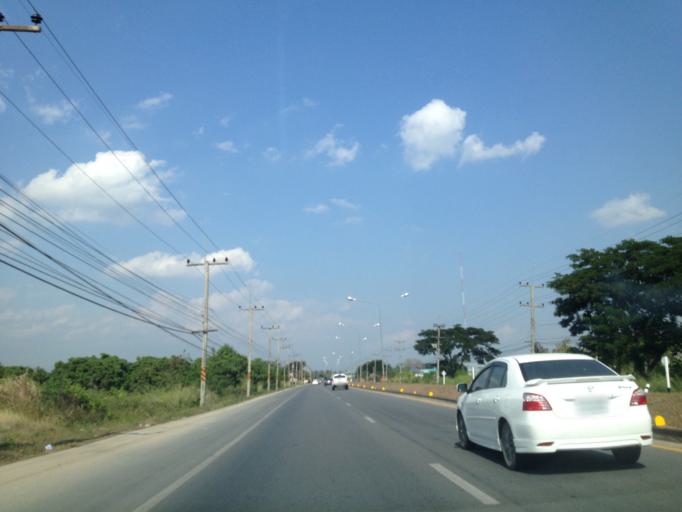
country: TH
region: Lamphun
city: Pa Sang
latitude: 18.5504
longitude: 98.8665
